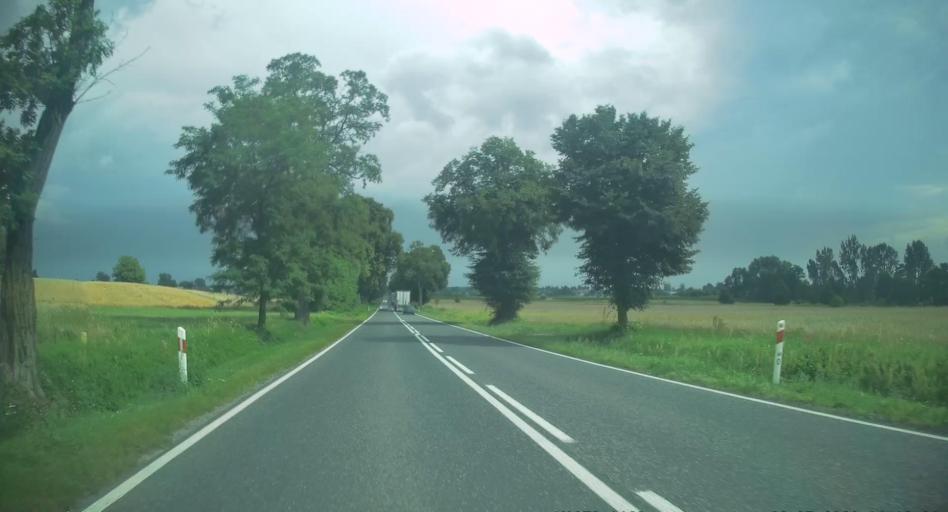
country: PL
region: Lodz Voivodeship
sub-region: Powiat skierniewicki
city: Gluchow
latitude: 51.7856
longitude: 20.0532
